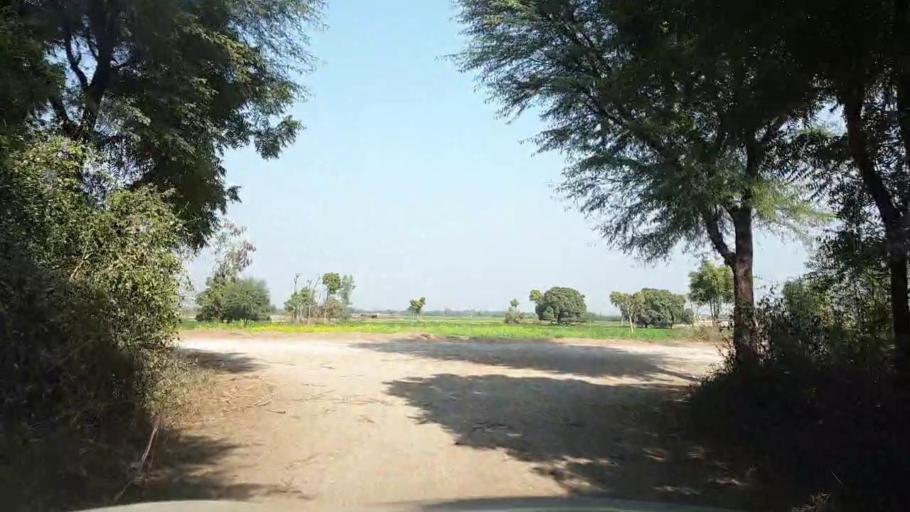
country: PK
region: Sindh
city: Bhit Shah
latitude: 25.7528
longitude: 68.4791
